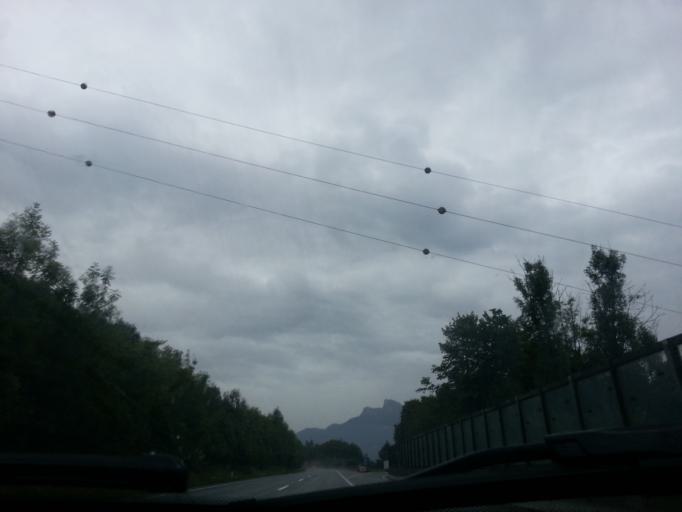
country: AT
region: Upper Austria
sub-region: Politischer Bezirk Vocklabruck
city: Mondsee
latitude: 47.8572
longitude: 13.3550
